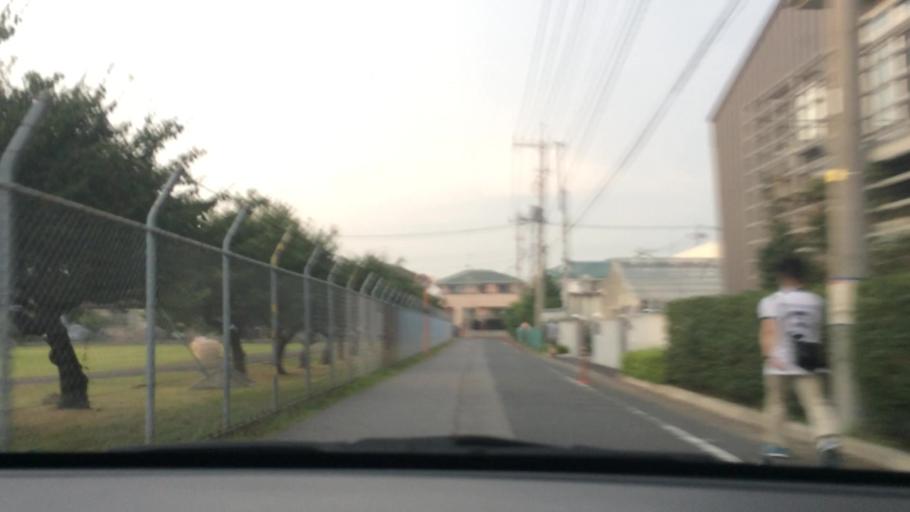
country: JP
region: Chiba
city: Kashiwa
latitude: 35.8889
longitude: 139.9399
